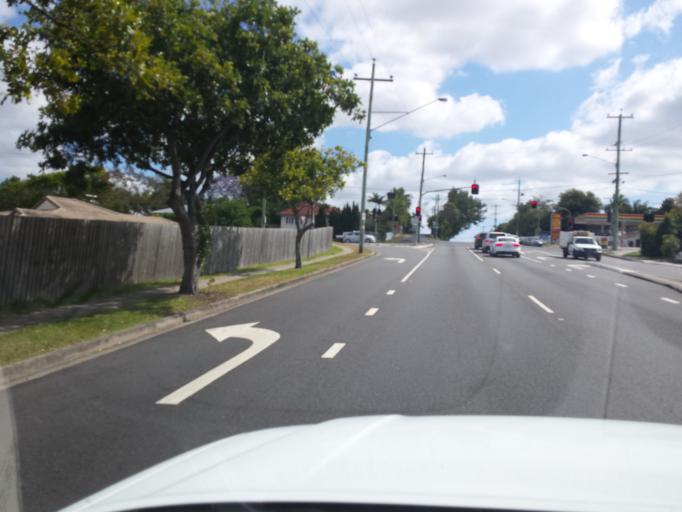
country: AU
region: Queensland
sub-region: Brisbane
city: Zillmere
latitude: -27.3675
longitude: 153.0366
